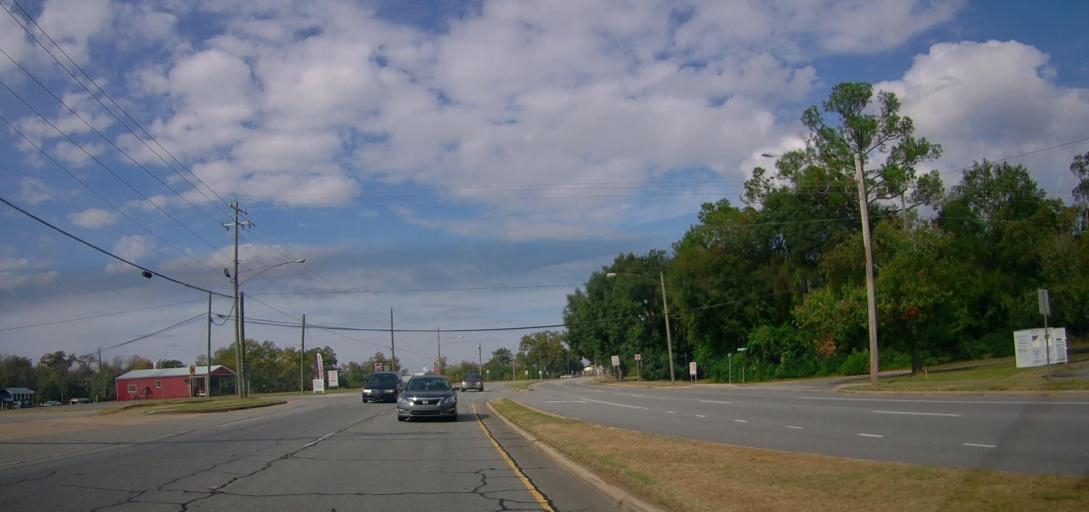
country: US
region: Georgia
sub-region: Mitchell County
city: Camilla
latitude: 31.2271
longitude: -84.1997
